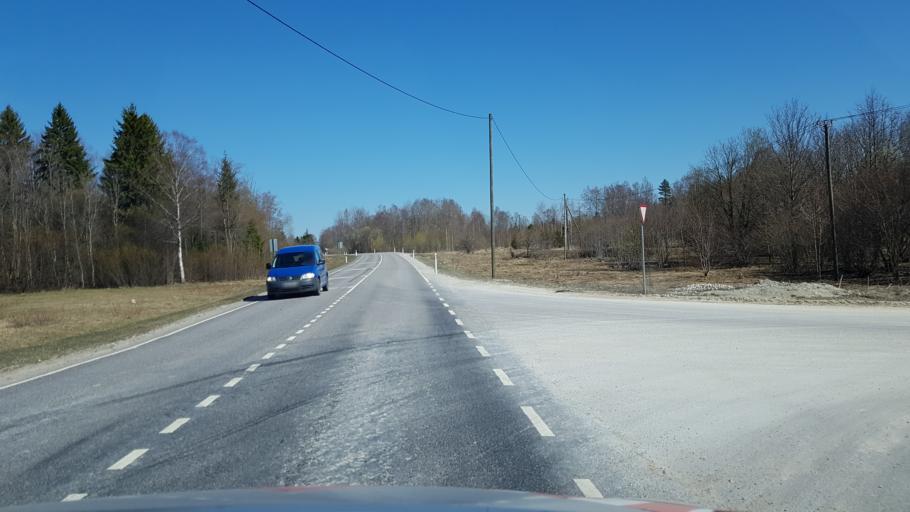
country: EE
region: Ida-Virumaa
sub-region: Kohtla-Jaerve linn
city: Kohtla-Jarve
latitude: 59.3297
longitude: 27.2730
